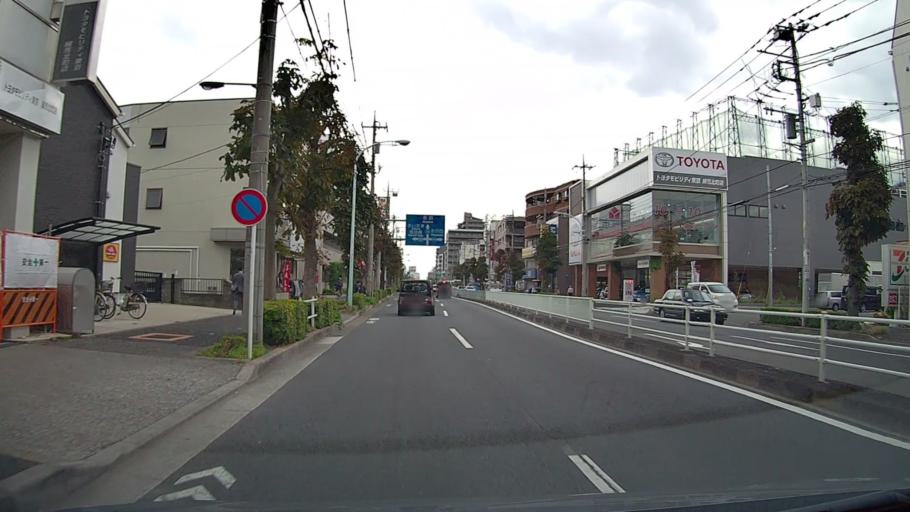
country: JP
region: Saitama
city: Wako
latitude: 35.7571
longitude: 139.6508
